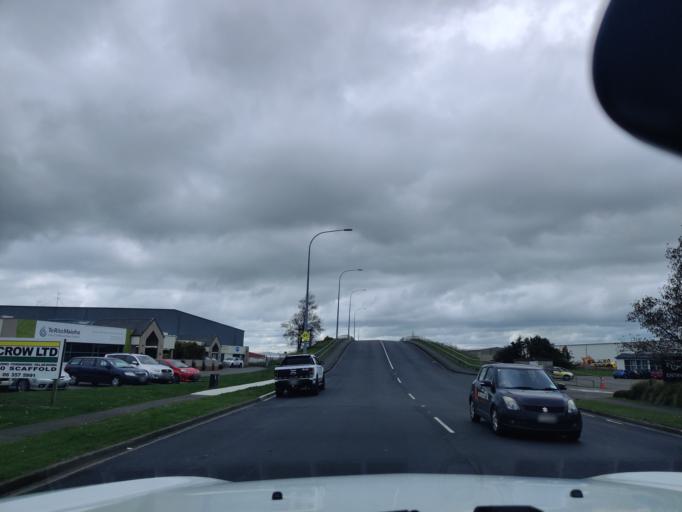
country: NZ
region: Manawatu-Wanganui
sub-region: Palmerston North City
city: Palmerston North
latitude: -40.3387
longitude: 175.6436
